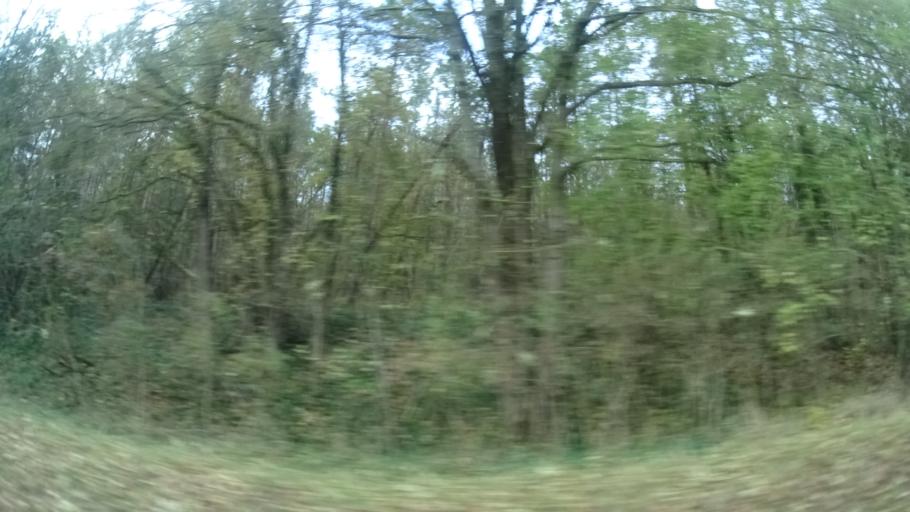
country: DE
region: Bavaria
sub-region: Regierungsbezirk Unterfranken
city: Aubstadt
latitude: 50.3408
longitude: 10.3947
